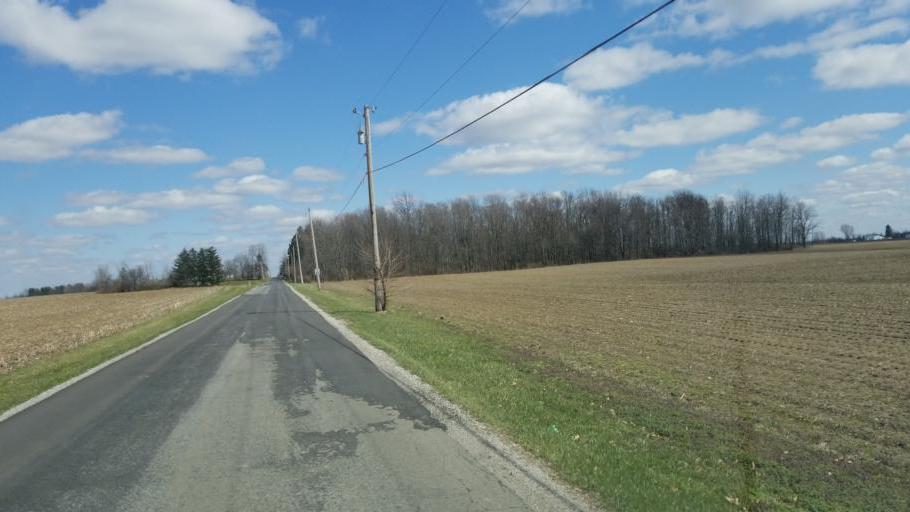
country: US
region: Ohio
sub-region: Richland County
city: Shelby
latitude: 40.8860
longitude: -82.6434
